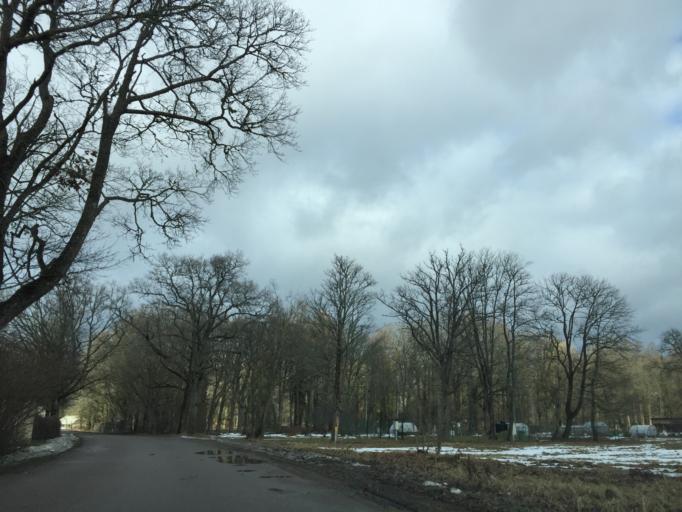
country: LV
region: Aloja
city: Aloja
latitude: 57.7710
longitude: 24.8123
